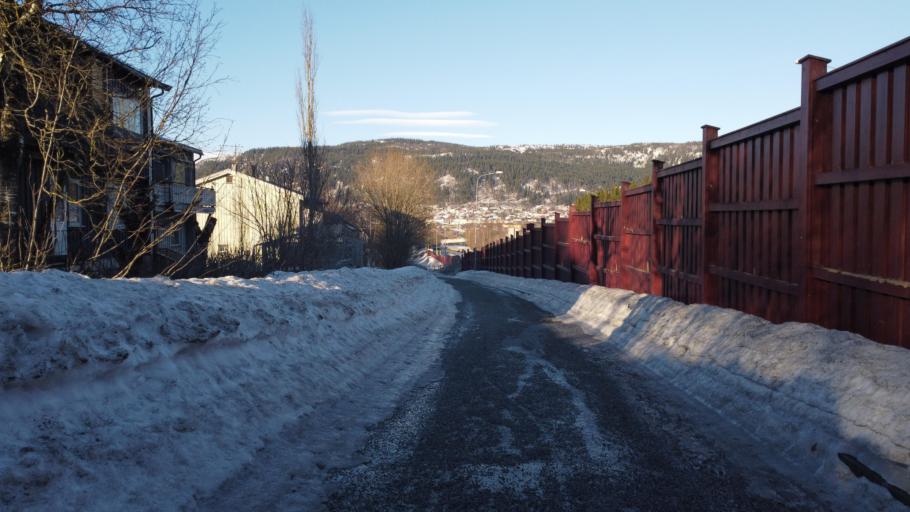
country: NO
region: Nordland
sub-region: Rana
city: Mo i Rana
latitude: 66.3152
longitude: 14.1667
